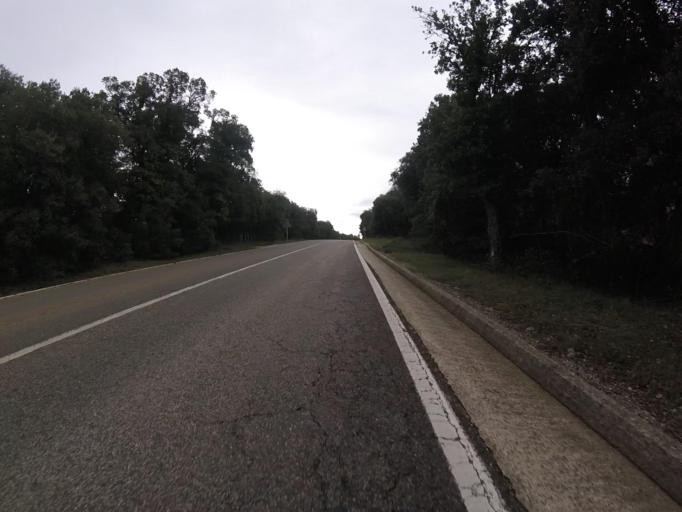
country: ES
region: Navarre
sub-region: Provincia de Navarra
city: Lezaun
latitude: 42.7581
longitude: -2.0123
